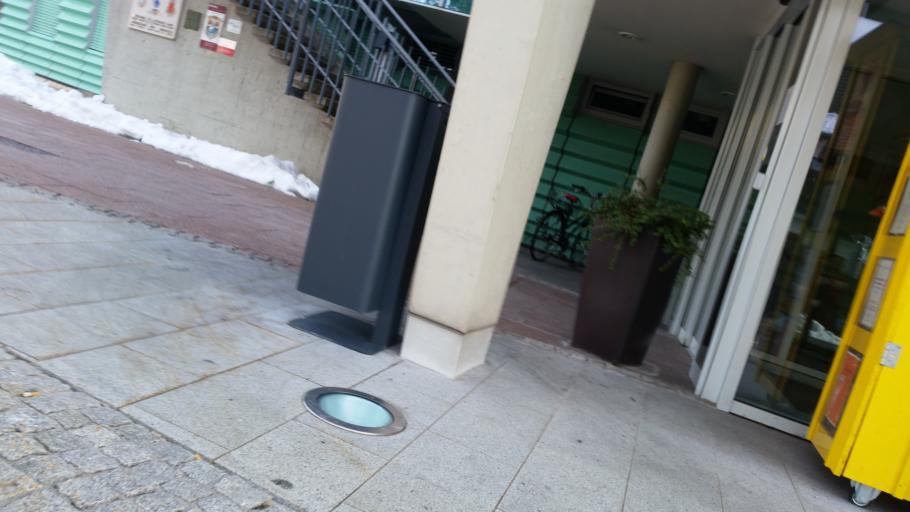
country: AT
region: Vorarlberg
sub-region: Politischer Bezirk Bregenz
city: Hard
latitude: 47.4888
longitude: 9.6911
